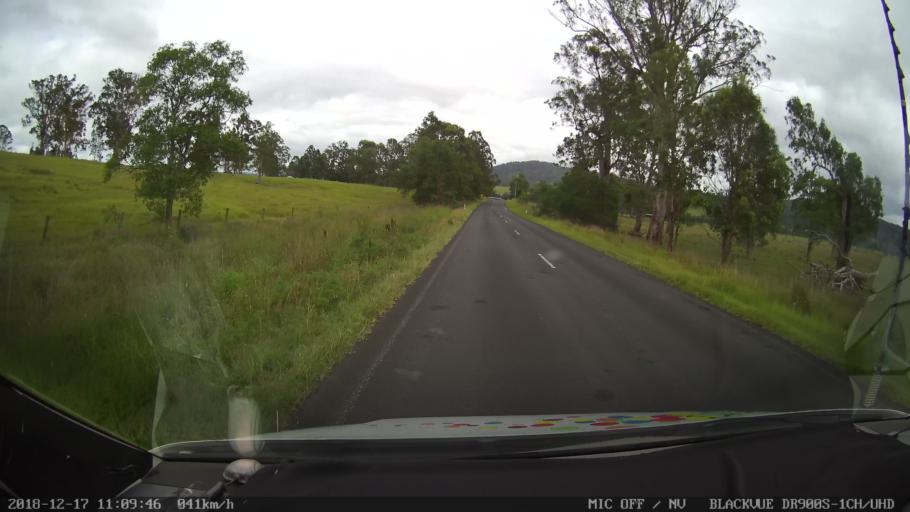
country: AU
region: New South Wales
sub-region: Kyogle
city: Kyogle
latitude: -28.7522
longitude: 152.6531
